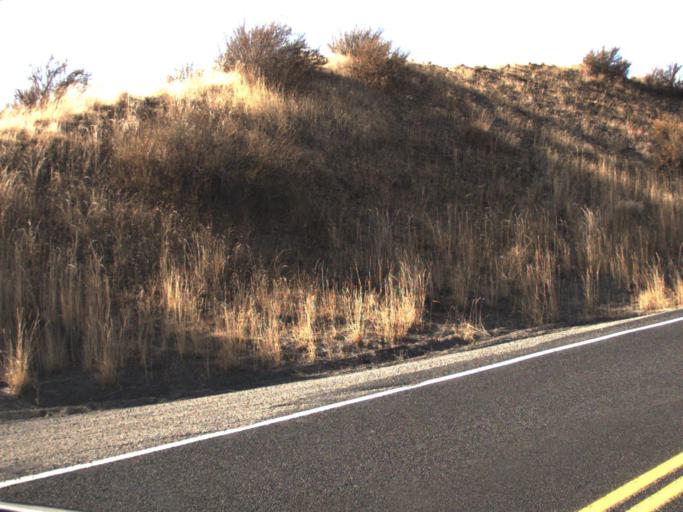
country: US
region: Washington
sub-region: Lincoln County
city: Davenport
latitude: 47.9065
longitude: -118.3336
